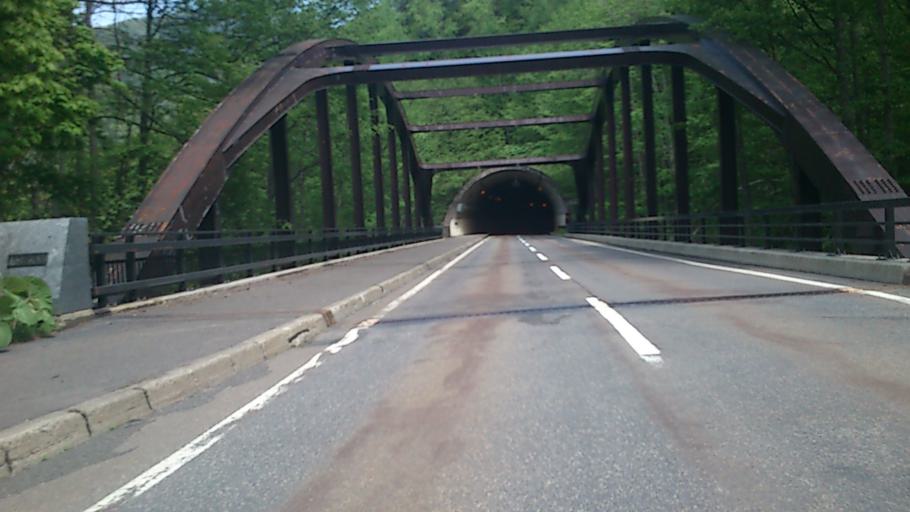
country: JP
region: Hokkaido
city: Otofuke
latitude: 43.3705
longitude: 143.2151
